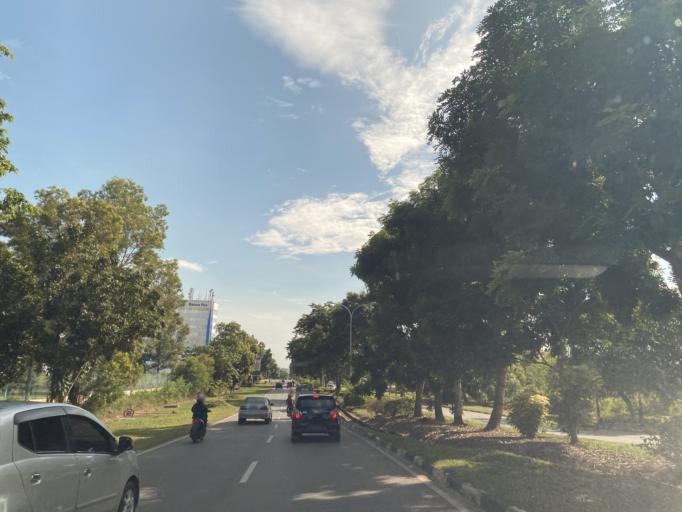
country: SG
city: Singapore
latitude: 1.1228
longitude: 104.0517
